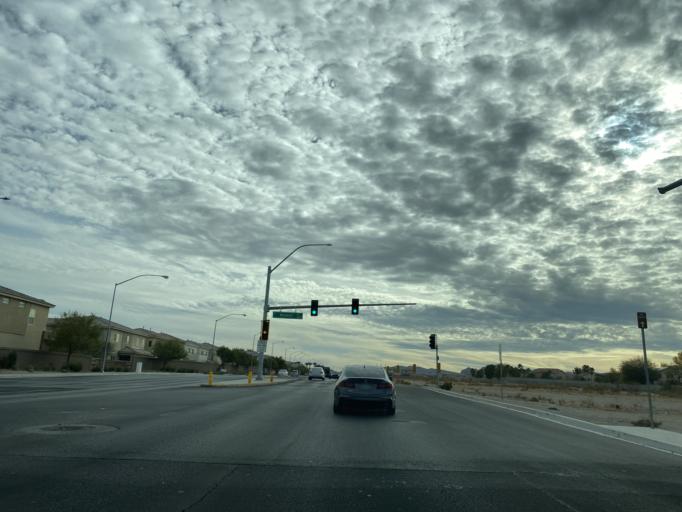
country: US
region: Nevada
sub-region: Clark County
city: Enterprise
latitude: 36.0411
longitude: -115.2791
